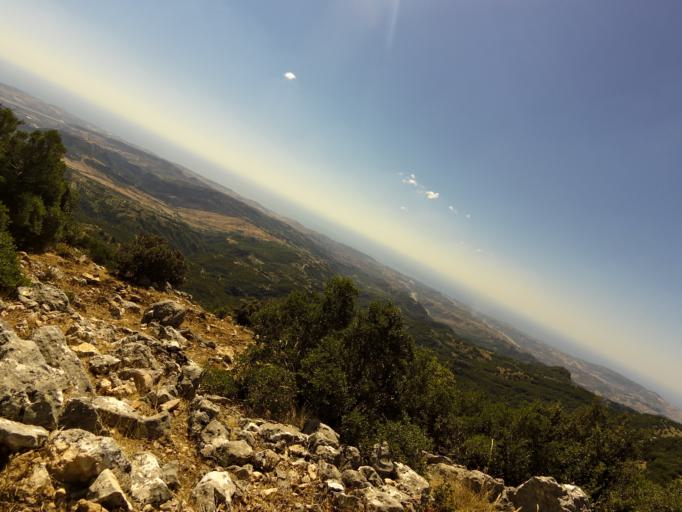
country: IT
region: Calabria
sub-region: Provincia di Reggio Calabria
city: Pazzano
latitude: 38.4546
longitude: 16.4263
